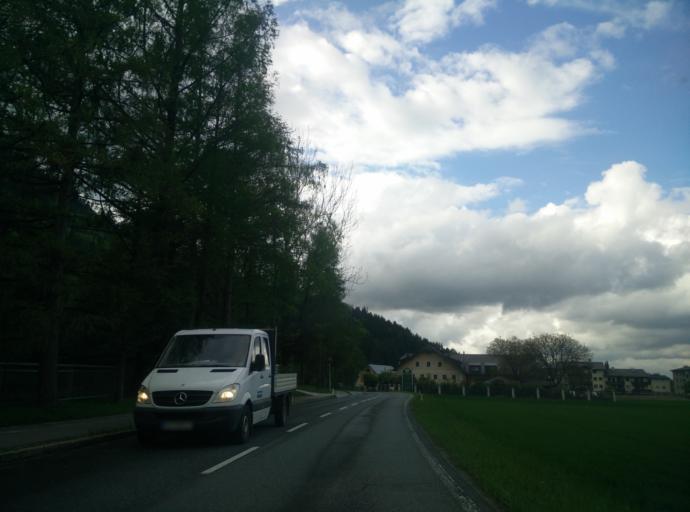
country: AT
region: Salzburg
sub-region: Politischer Bezirk Salzburg-Umgebung
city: Grodig
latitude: 47.7297
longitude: 13.0401
